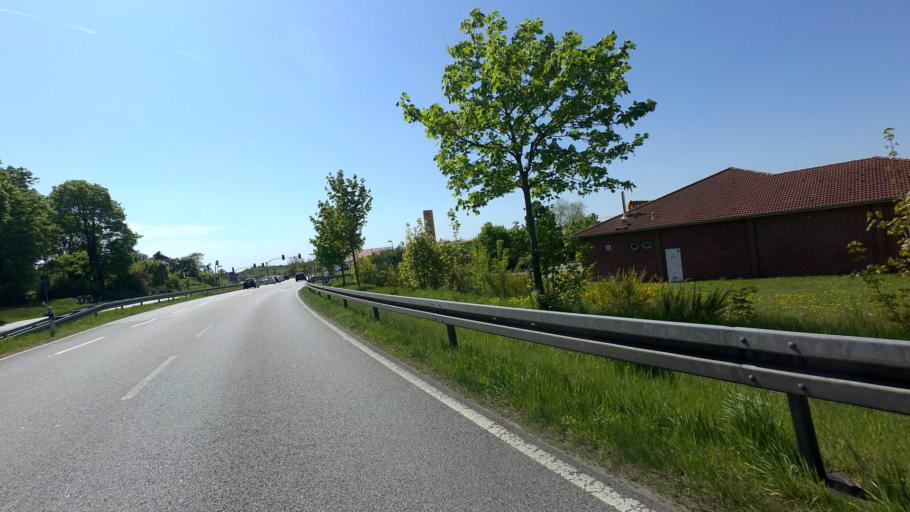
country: DE
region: Brandenburg
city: Konigs Wusterhausen
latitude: 52.3037
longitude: 13.6025
